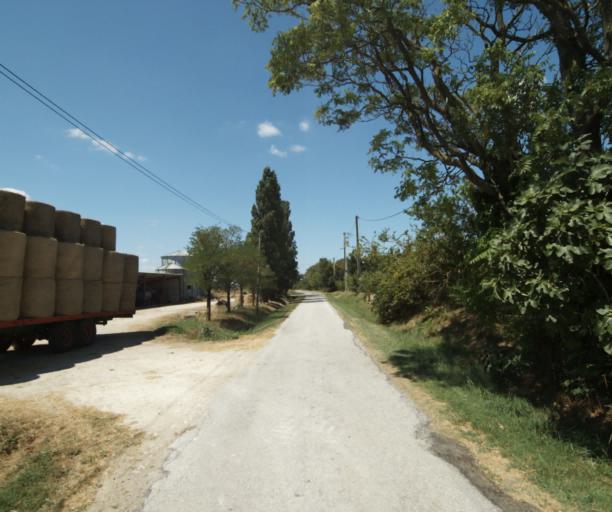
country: FR
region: Midi-Pyrenees
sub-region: Departement de la Haute-Garonne
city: Saint-Felix-Lauragais
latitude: 43.4820
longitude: 1.8660
